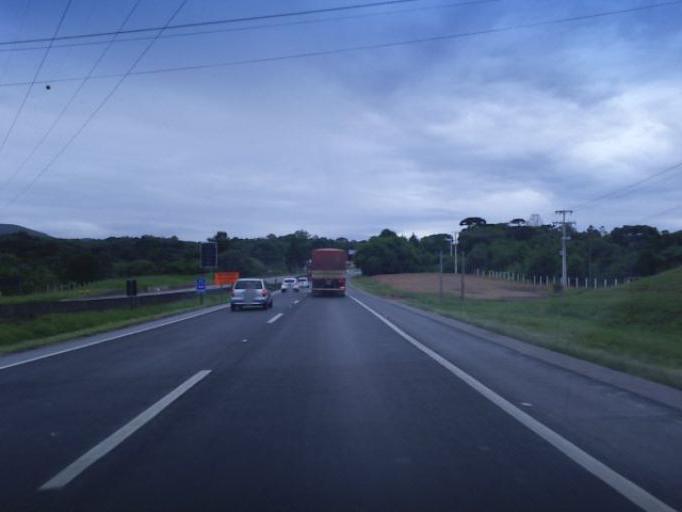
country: BR
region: Parana
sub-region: Sao Jose Dos Pinhais
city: Sao Jose dos Pinhais
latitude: -25.7368
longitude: -49.1312
